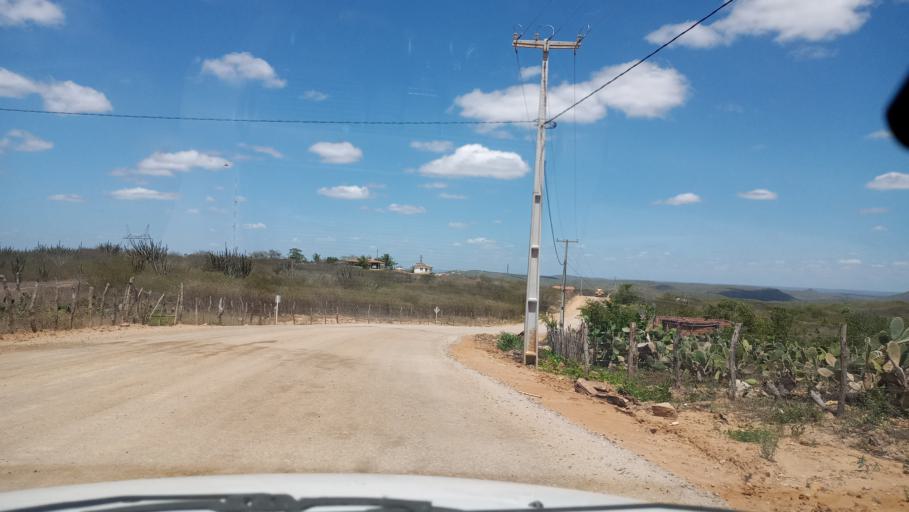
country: BR
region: Rio Grande do Norte
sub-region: Sao Paulo Do Potengi
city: Sao Paulo do Potengi
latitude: -5.7760
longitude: -35.9140
